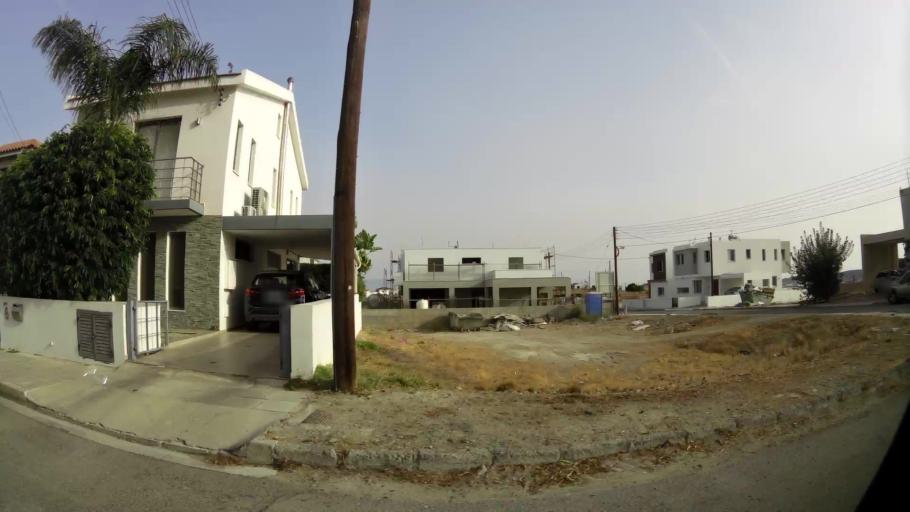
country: CY
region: Lefkosia
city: Geri
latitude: 35.0675
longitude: 33.3898
